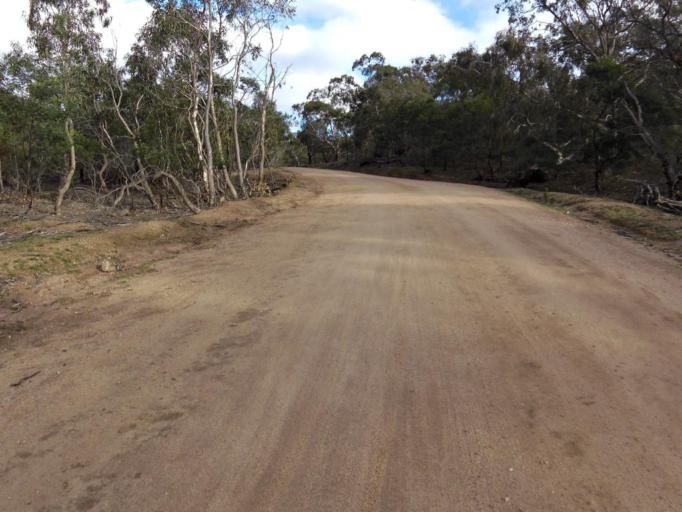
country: AU
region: Victoria
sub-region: Wyndham
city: Little River
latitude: -37.9335
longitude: 144.4410
